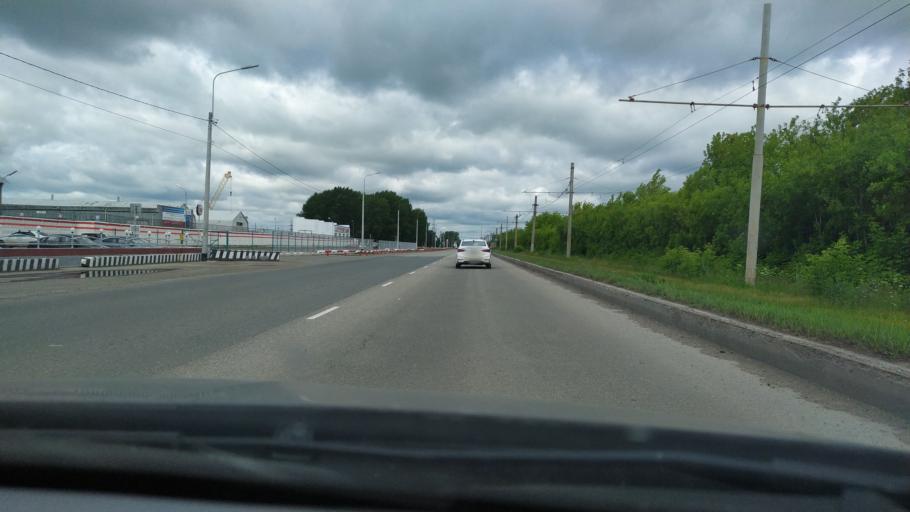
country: RU
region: Perm
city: Kondratovo
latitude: 57.9273
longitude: 56.1338
